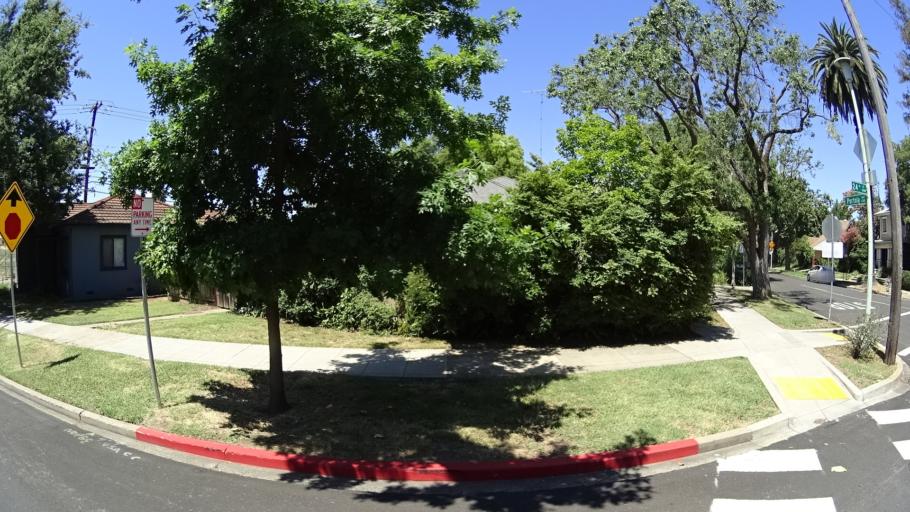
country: US
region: California
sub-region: Sacramento County
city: Sacramento
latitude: 38.5499
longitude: -121.4836
